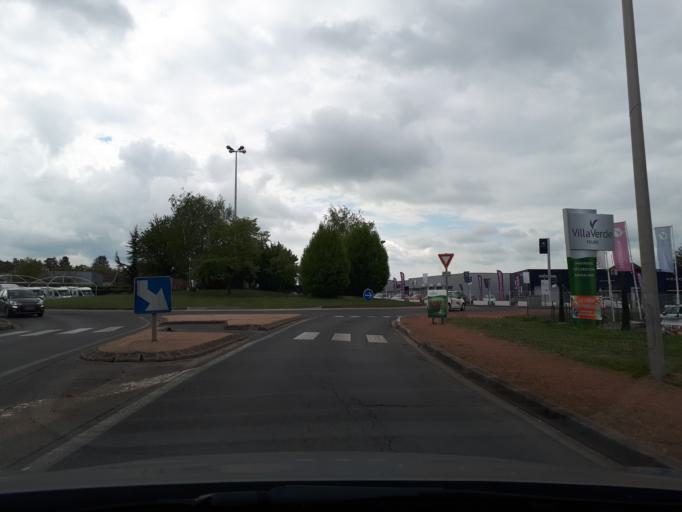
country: FR
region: Rhone-Alpes
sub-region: Departement de la Loire
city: Feurs
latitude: 45.7289
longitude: 4.2255
